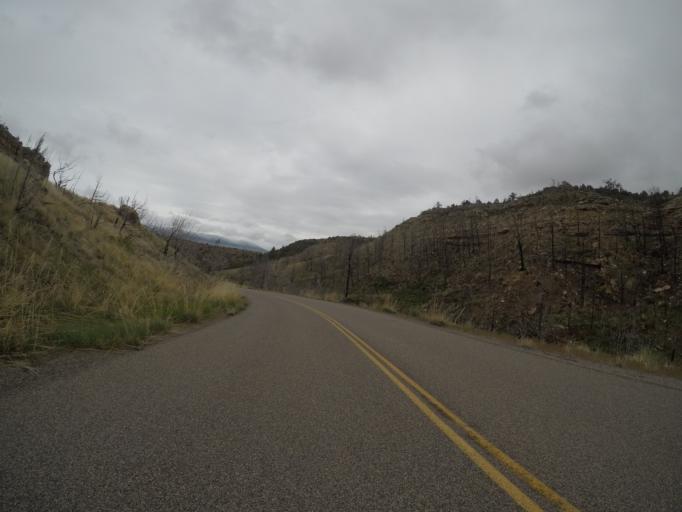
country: US
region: Wyoming
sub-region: Big Horn County
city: Lovell
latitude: 45.1081
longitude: -108.2342
